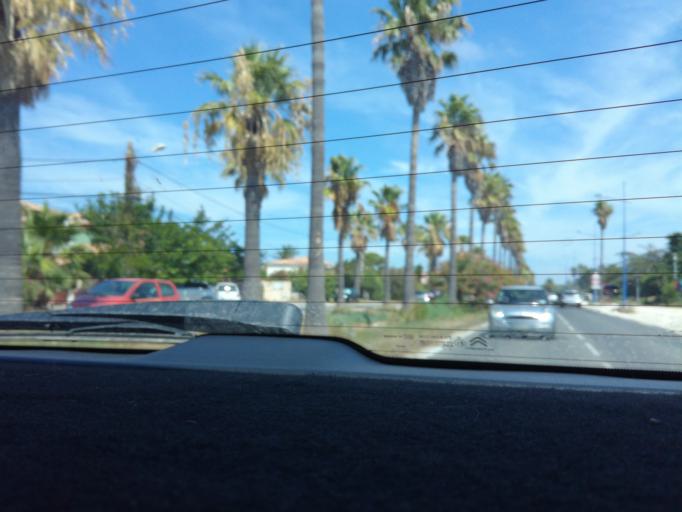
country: FR
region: Provence-Alpes-Cote d'Azur
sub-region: Departement du Var
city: Hyeres
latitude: 43.0453
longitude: 6.1461
